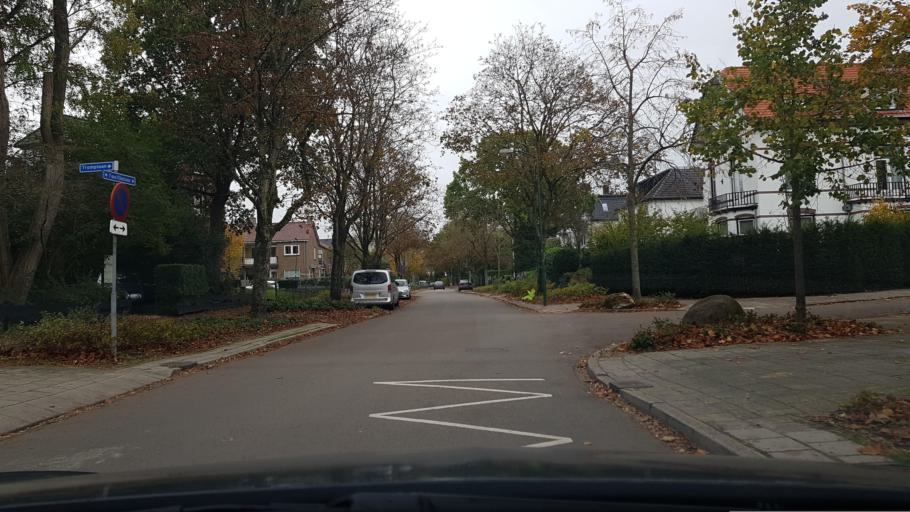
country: NL
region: Utrecht
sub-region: Gemeente Baarn
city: Baarn
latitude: 52.2099
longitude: 5.2975
